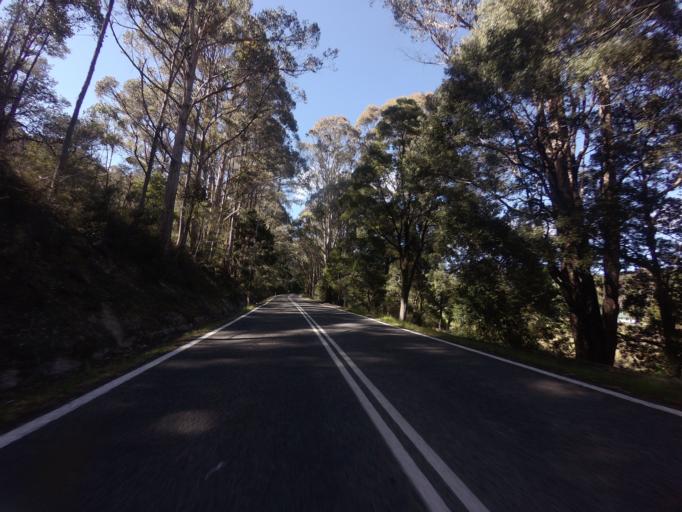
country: AU
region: Tasmania
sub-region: Derwent Valley
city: New Norfolk
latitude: -42.6983
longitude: 146.7133
